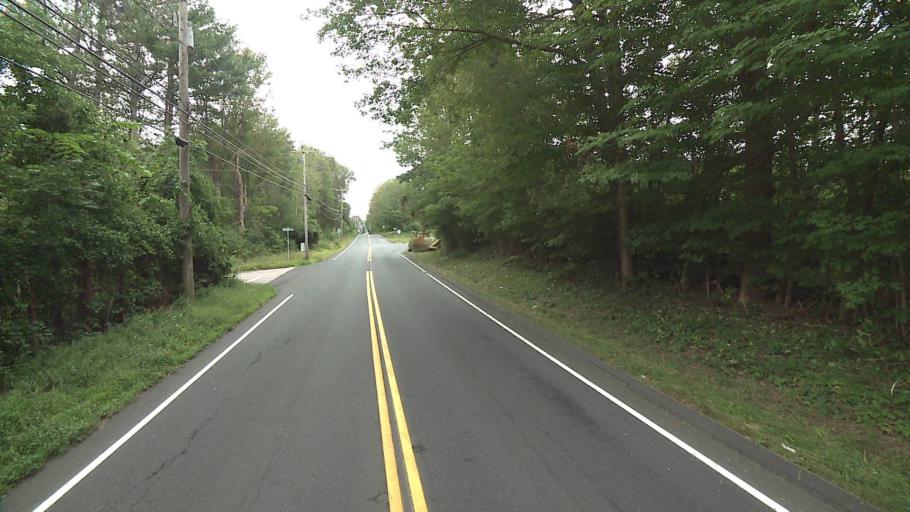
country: US
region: Connecticut
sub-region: New London County
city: Colchester
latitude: 41.5568
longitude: -72.3159
